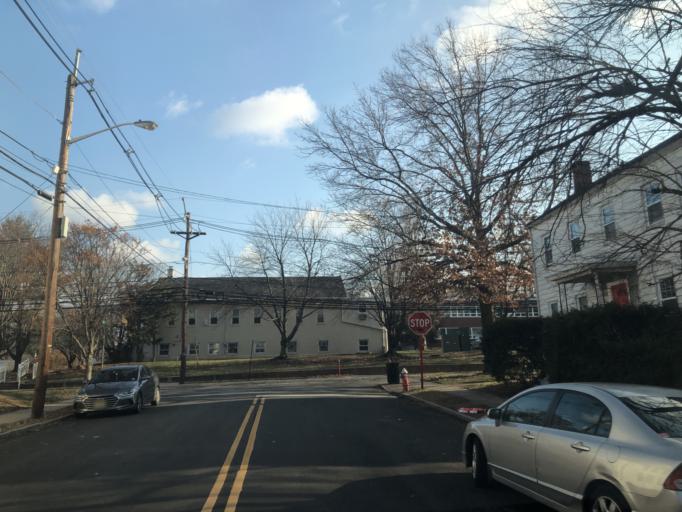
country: US
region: New Jersey
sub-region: Middlesex County
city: New Brunswick
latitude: 40.4828
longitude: -74.4403
